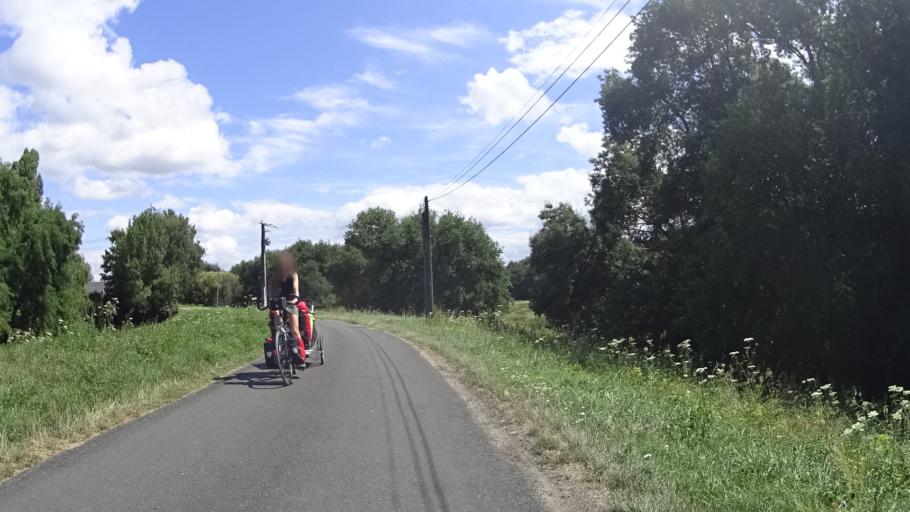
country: FR
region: Centre
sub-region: Departement d'Indre-et-Loire
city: Cinq-Mars-la-Pile
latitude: 47.3382
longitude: 0.4752
